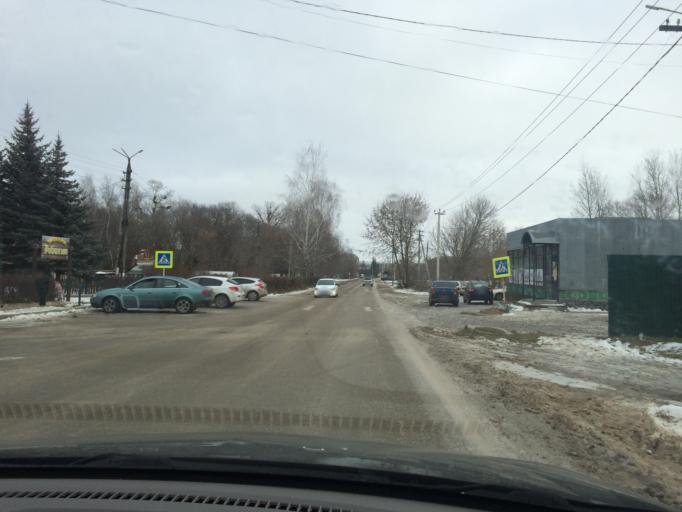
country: RU
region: Tula
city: Plavsk
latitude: 53.7039
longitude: 37.2828
